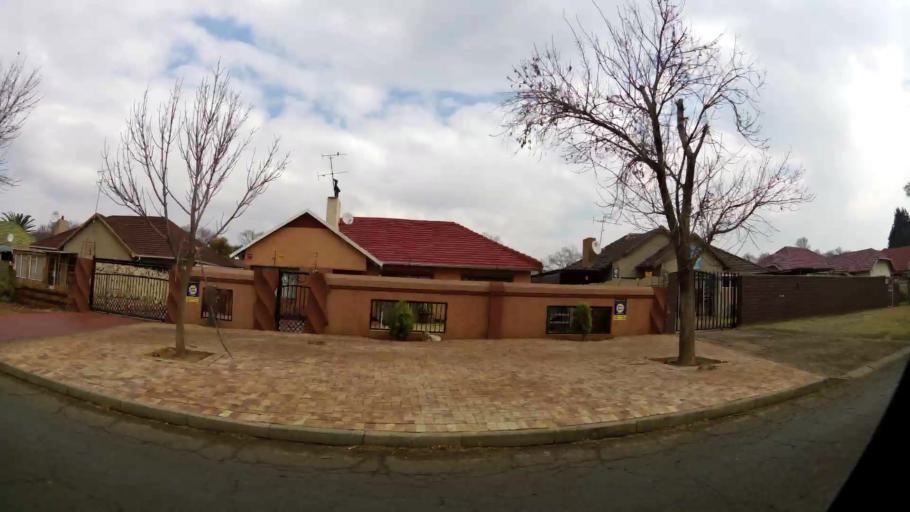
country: ZA
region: Gauteng
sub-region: Sedibeng District Municipality
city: Vanderbijlpark
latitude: -26.6993
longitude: 27.8476
